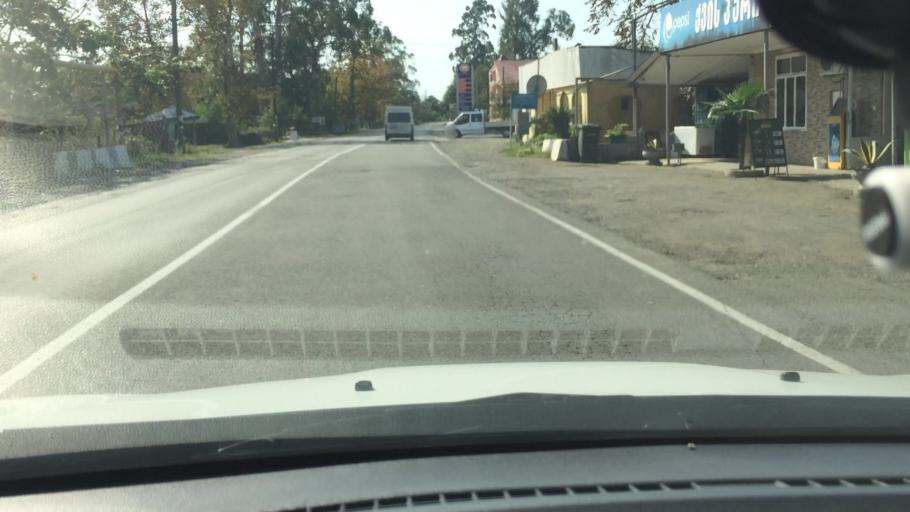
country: GE
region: Guria
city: Urek'i
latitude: 42.0087
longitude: 41.7807
